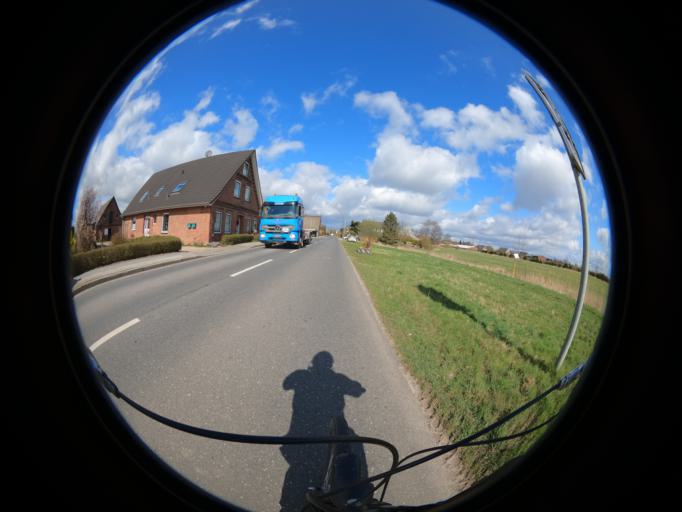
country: DE
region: Lower Saxony
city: Neu Wulmstorf
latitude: 53.5128
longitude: 9.7918
